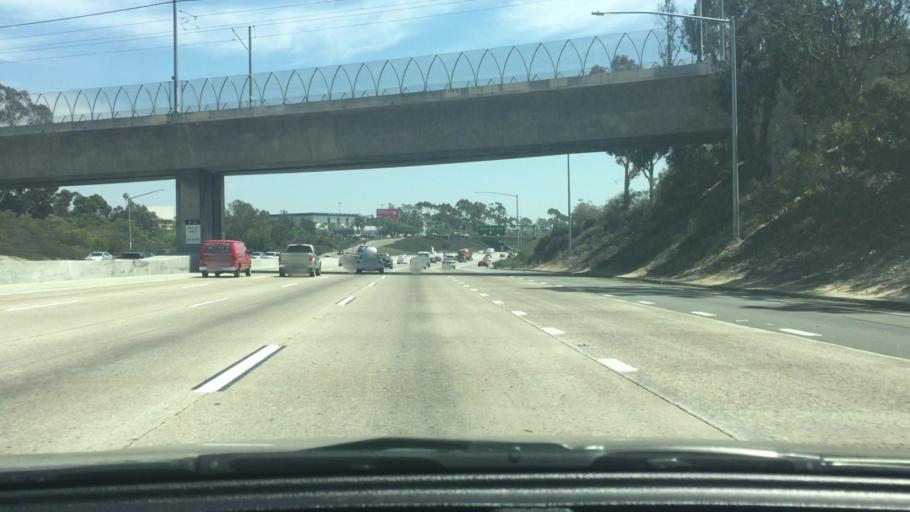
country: US
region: California
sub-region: San Diego County
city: National City
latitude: 32.7081
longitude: -117.0977
